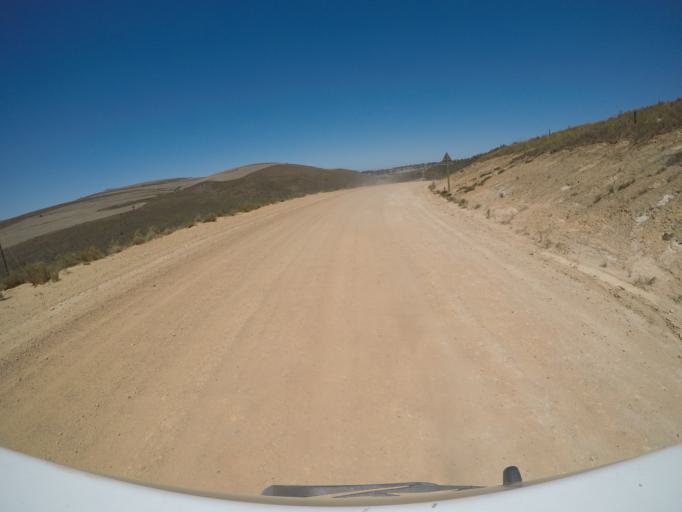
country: ZA
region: Western Cape
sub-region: Overberg District Municipality
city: Grabouw
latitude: -34.2059
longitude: 19.2160
